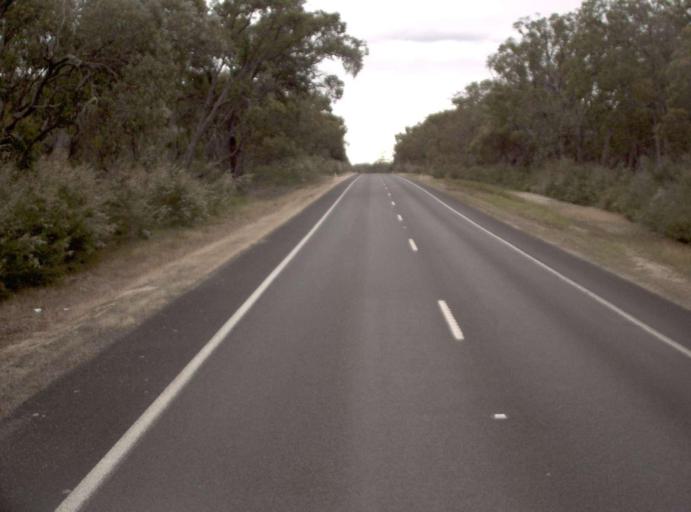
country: AU
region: Victoria
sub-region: Wellington
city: Sale
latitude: -38.3362
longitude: 147.0124
